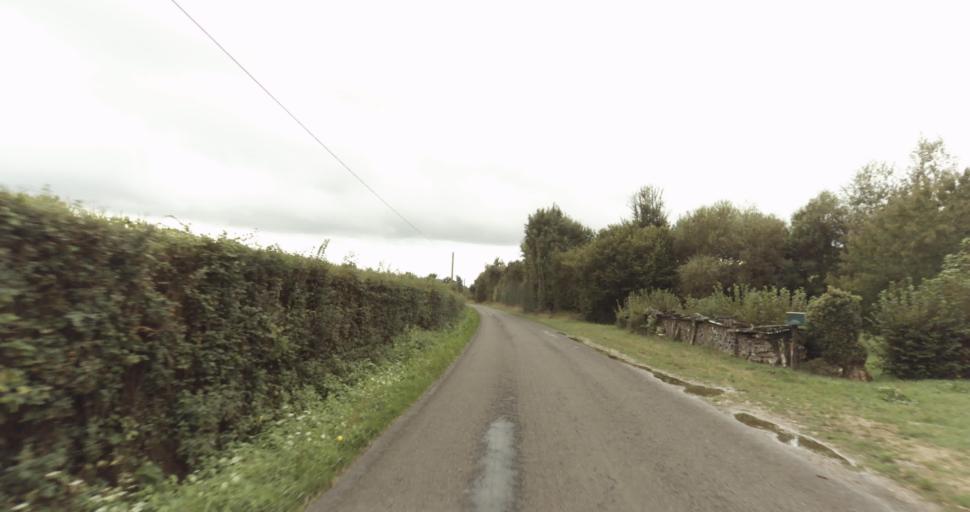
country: FR
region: Lower Normandy
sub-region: Departement de l'Orne
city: Vimoutiers
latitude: 48.8949
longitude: 0.1817
